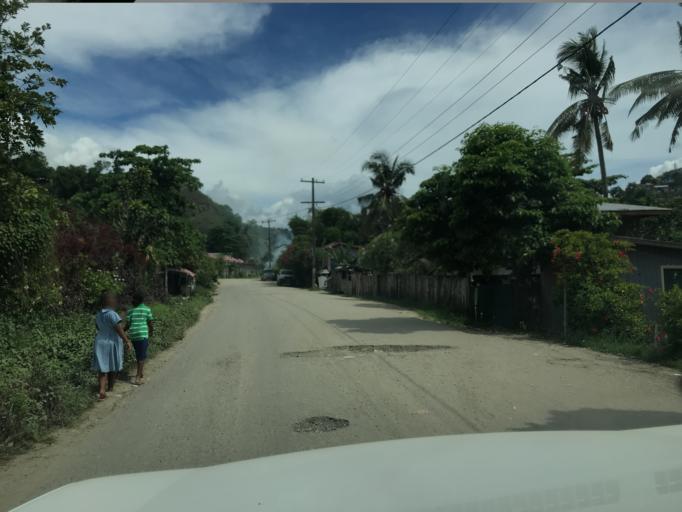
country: SB
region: Guadalcanal
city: Honiara
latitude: -9.4404
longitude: 159.9615
